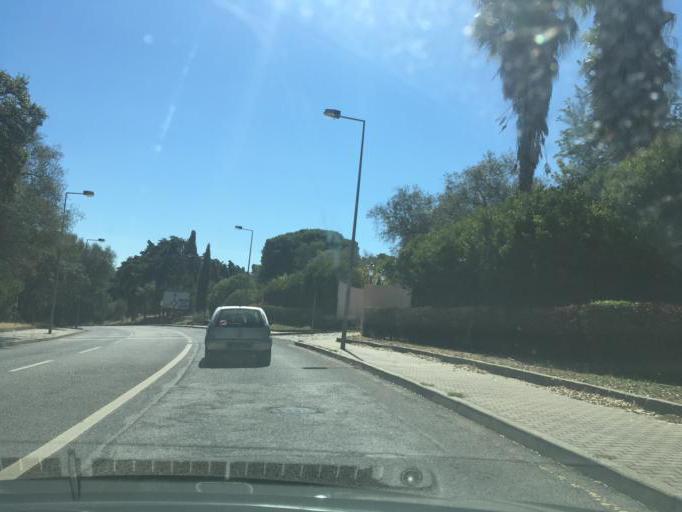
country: PT
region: Lisbon
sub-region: Oeiras
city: Alges
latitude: 38.7161
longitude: -9.2009
